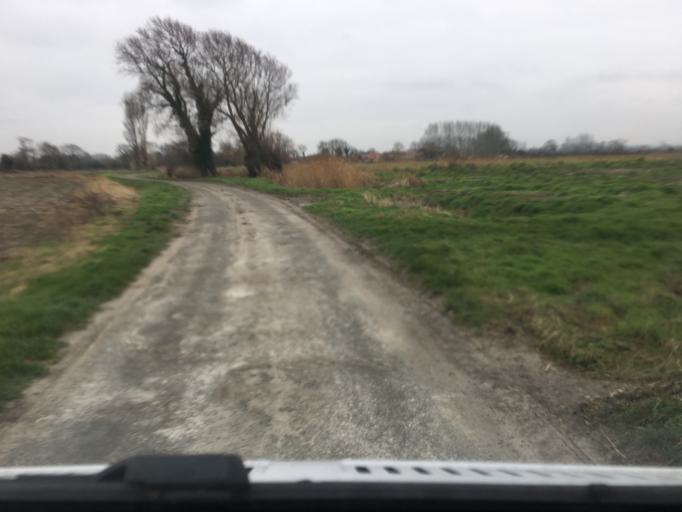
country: FR
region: Picardie
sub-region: Departement de la Somme
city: Pende
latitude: 50.1759
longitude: 1.5433
